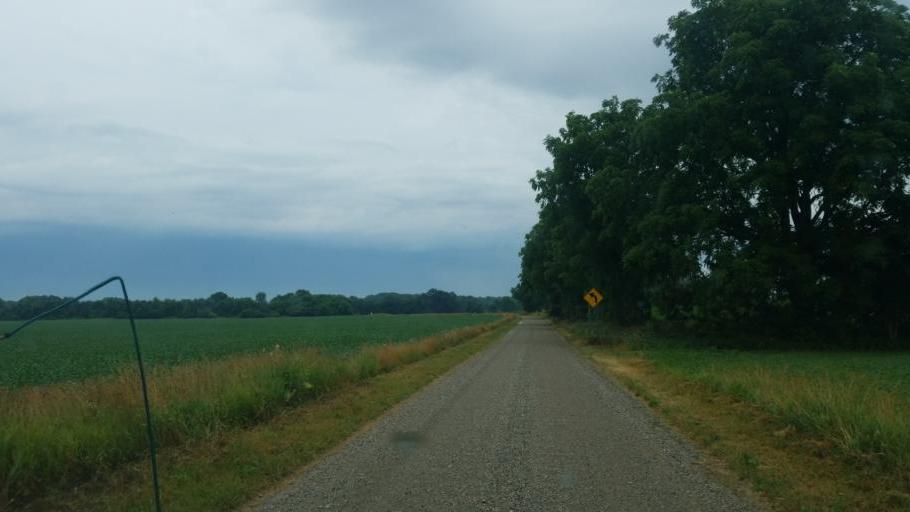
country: US
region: Indiana
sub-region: Steuben County
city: Hamilton
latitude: 41.5051
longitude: -84.9280
